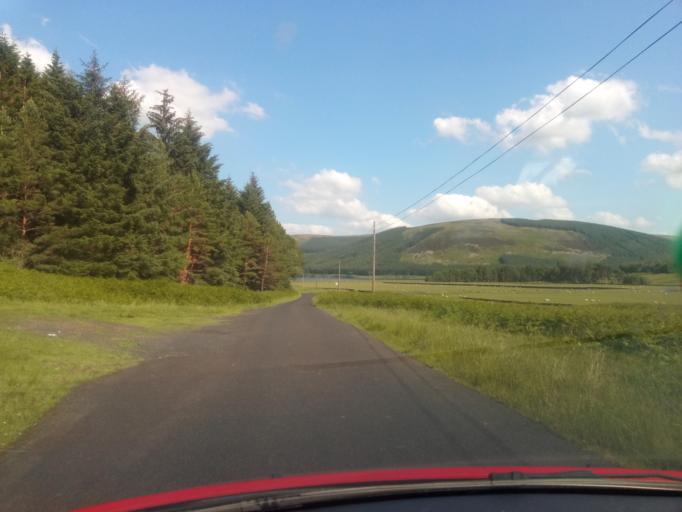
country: GB
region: Scotland
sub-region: The Scottish Borders
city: Peebles
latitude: 55.4963
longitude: -3.2123
